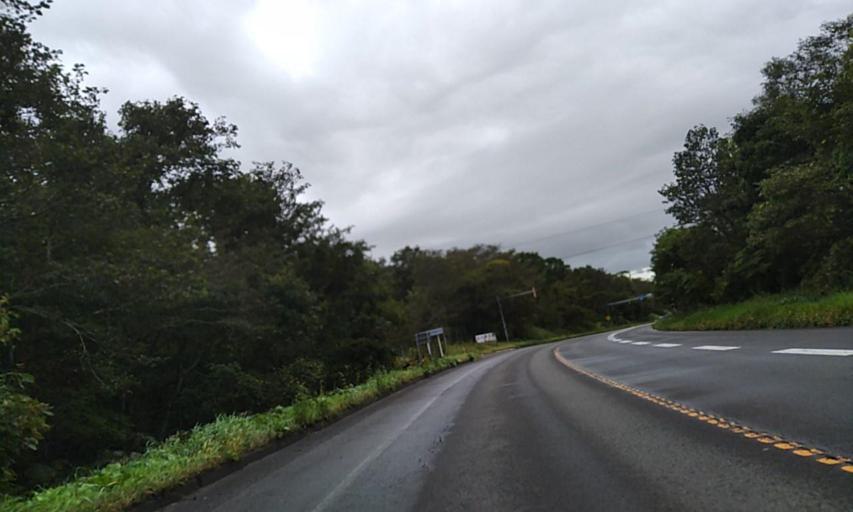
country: JP
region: Hokkaido
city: Kushiro
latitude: 42.9284
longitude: 144.0147
